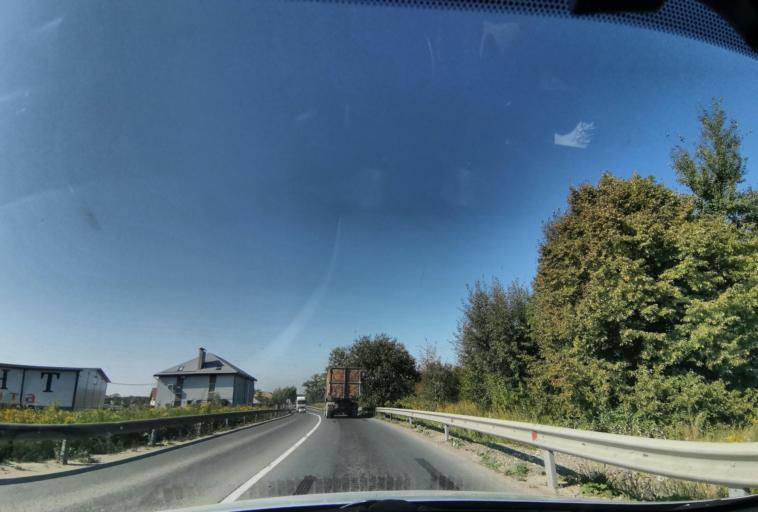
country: RU
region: Kaliningrad
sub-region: Gorod Kaliningrad
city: Kaliningrad
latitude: 54.7699
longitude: 20.4976
